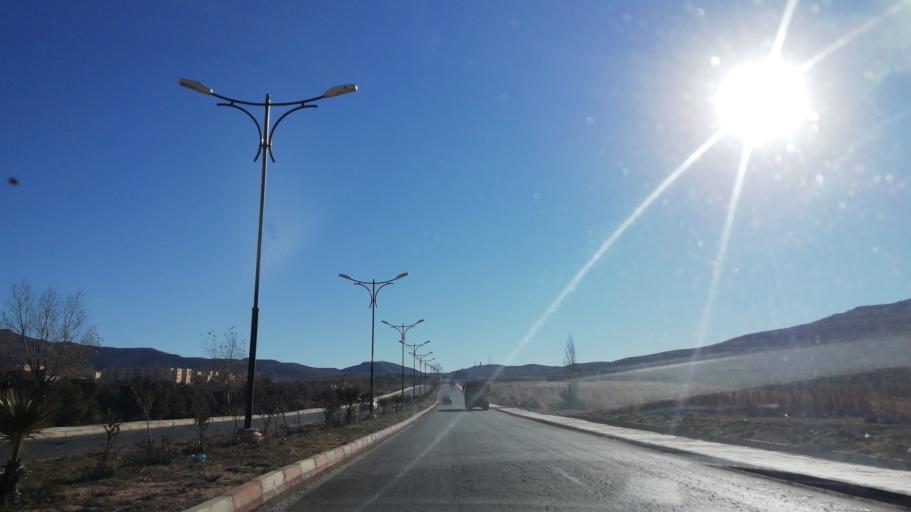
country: DZ
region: El Bayadh
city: El Bayadh
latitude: 33.6596
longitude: 1.0613
